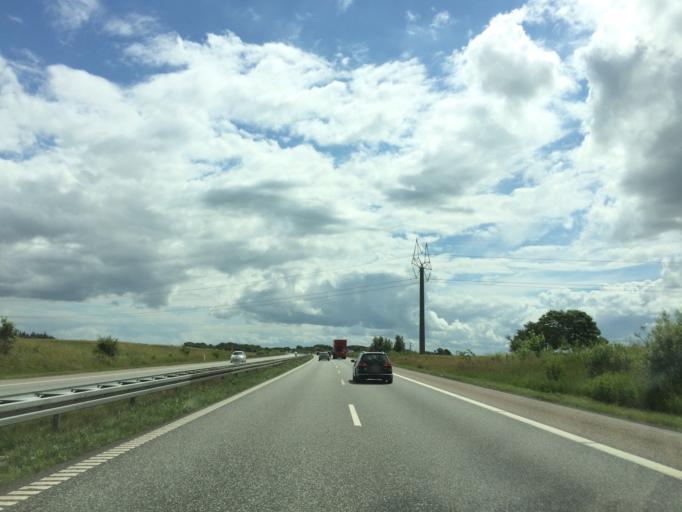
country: DK
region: North Denmark
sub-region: Mariagerfjord Kommune
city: Hobro
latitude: 56.7444
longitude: 9.6977
